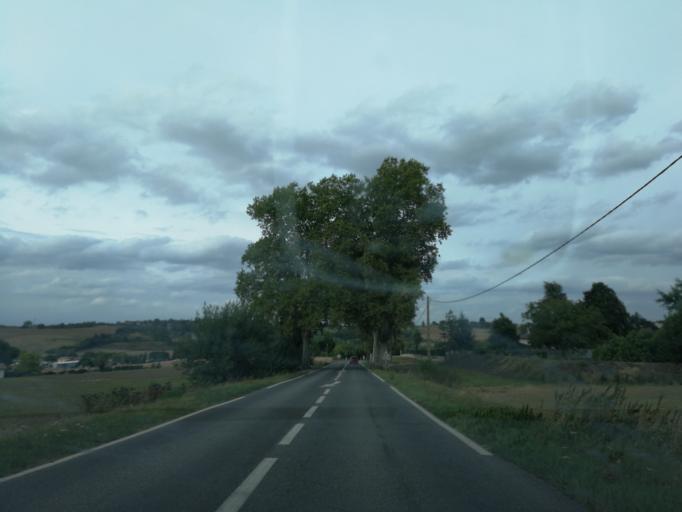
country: FR
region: Midi-Pyrenees
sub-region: Departement de la Haute-Garonne
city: Dremil-Lafage
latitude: 43.5903
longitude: 1.5866
